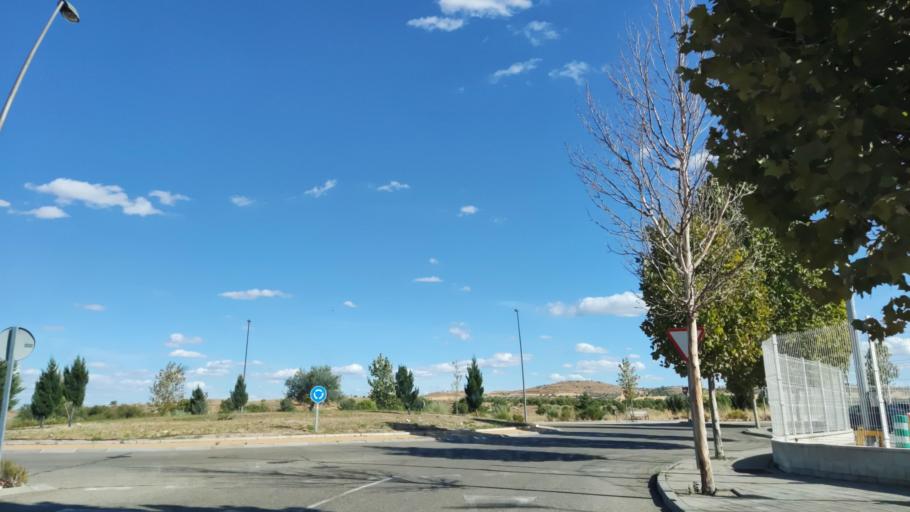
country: ES
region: Madrid
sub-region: Provincia de Madrid
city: Pinto
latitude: 40.2806
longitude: -3.6748
